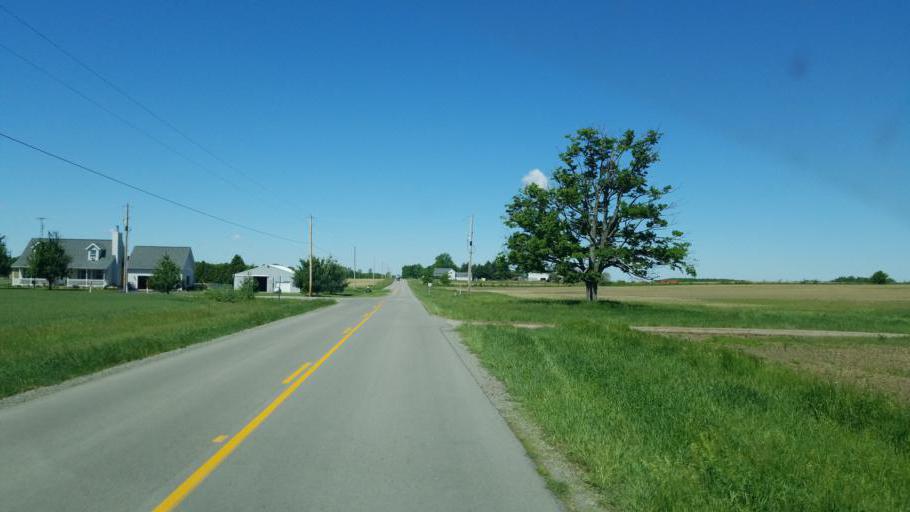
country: US
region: Ohio
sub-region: Logan County
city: Russells Point
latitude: 40.4257
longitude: -83.8385
